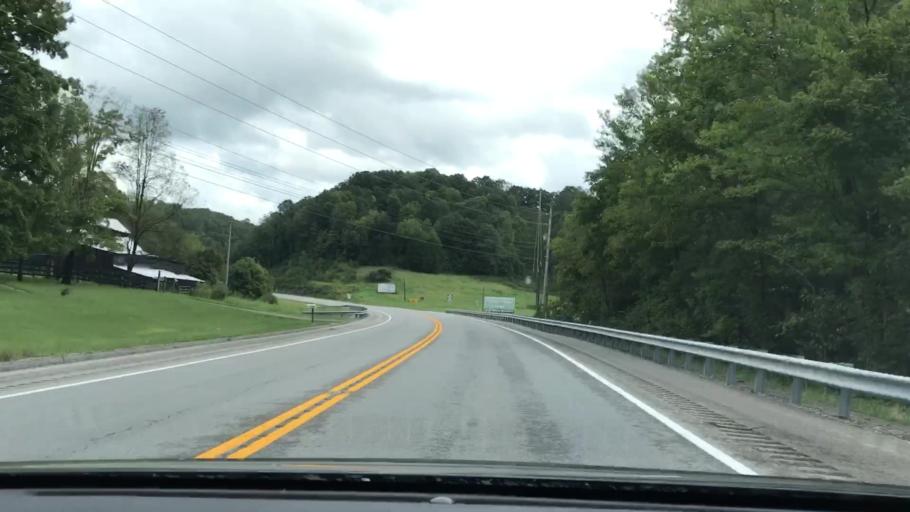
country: US
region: Kentucky
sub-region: Cumberland County
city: Burkesville
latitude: 36.7952
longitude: -85.3924
